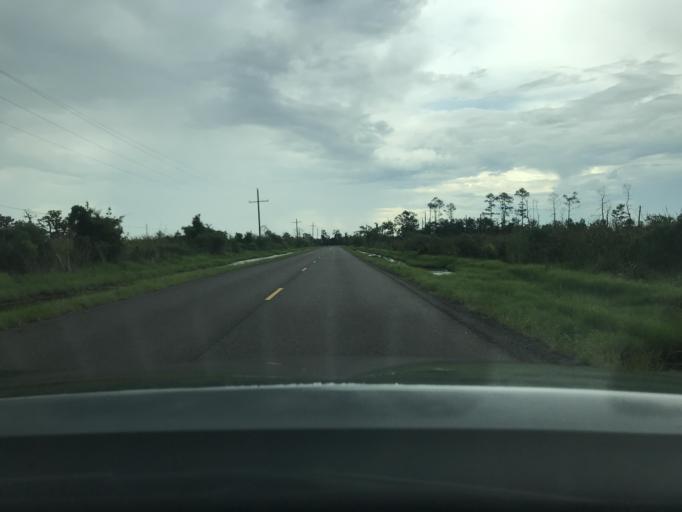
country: US
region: Louisiana
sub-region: Calcasieu Parish
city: Westlake
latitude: 30.2570
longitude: -93.2228
